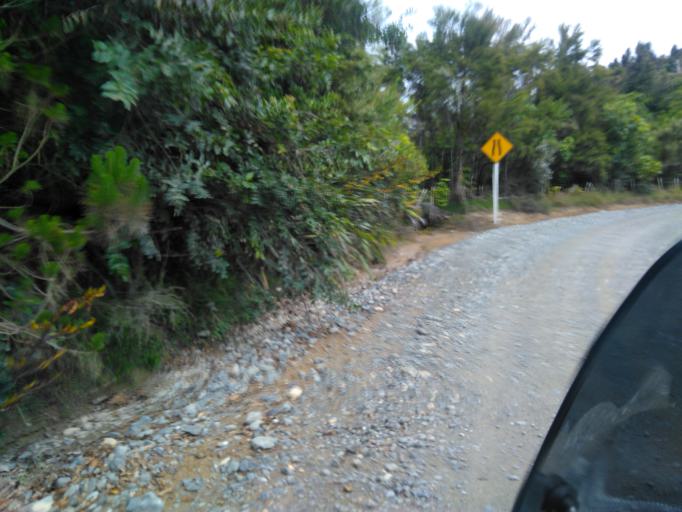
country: NZ
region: Gisborne
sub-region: Gisborne District
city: Gisborne
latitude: -38.2354
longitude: 178.0664
